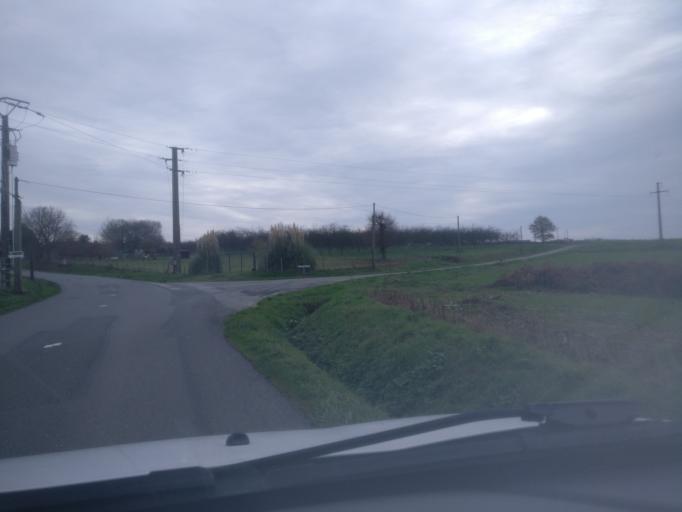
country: FR
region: Brittany
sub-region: Departement d'Ille-et-Vilaine
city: Liffre
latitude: 48.1825
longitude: -1.4963
